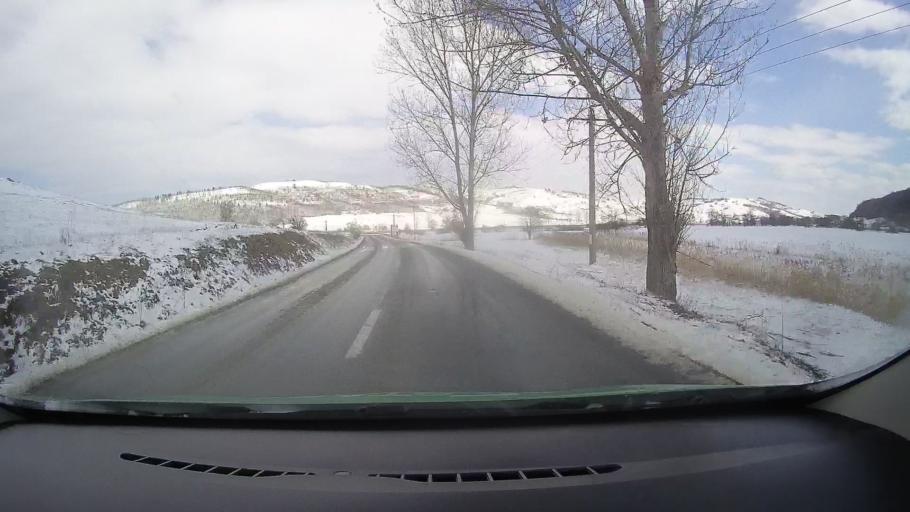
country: RO
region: Sibiu
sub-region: Comuna Altina
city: Altina
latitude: 45.9642
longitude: 24.4679
